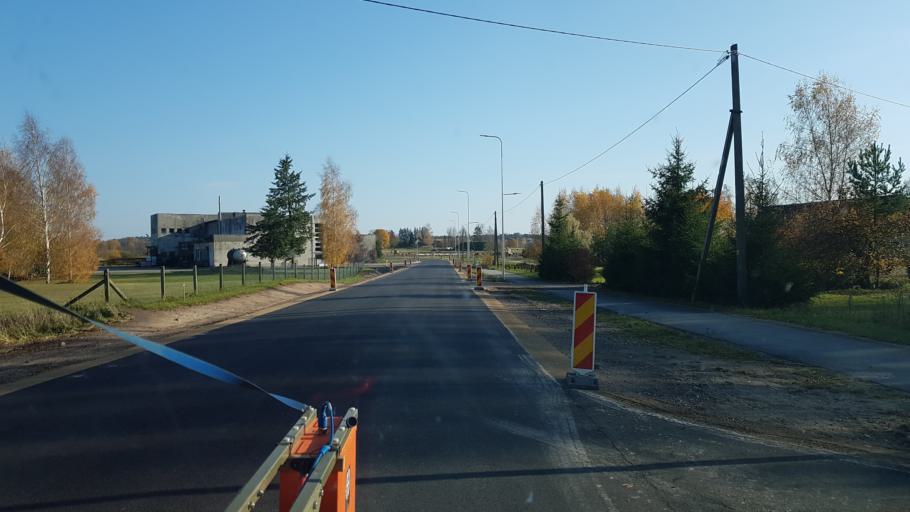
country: EE
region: Vorumaa
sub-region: Antsla vald
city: Vana-Antsla
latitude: 57.8412
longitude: 26.4795
